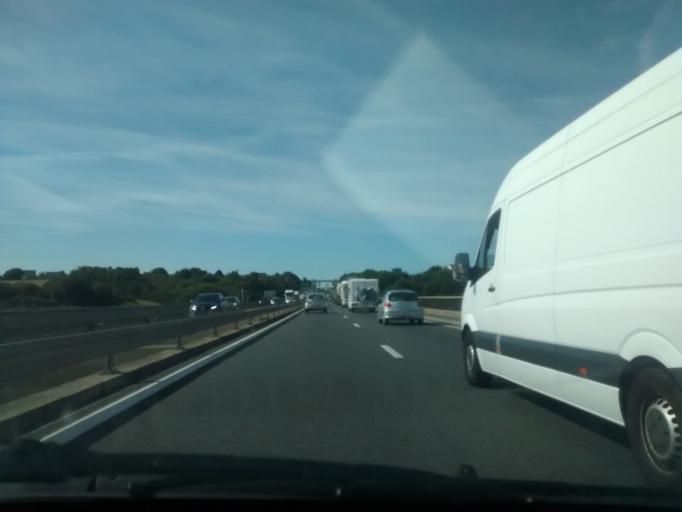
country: FR
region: Brittany
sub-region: Departement des Cotes-d'Armor
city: Saint-Brieuc
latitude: 48.5244
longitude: -2.7508
